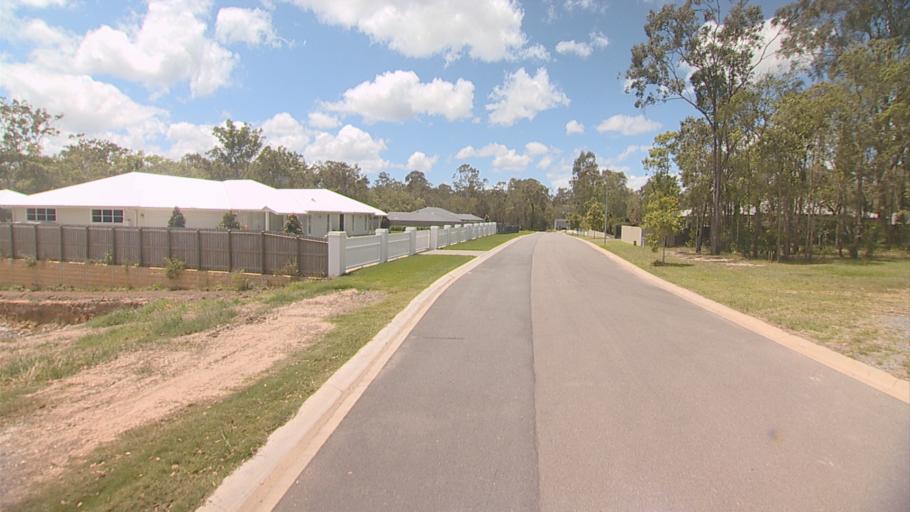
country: AU
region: Queensland
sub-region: Logan
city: Beenleigh
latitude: -27.6654
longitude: 153.2192
